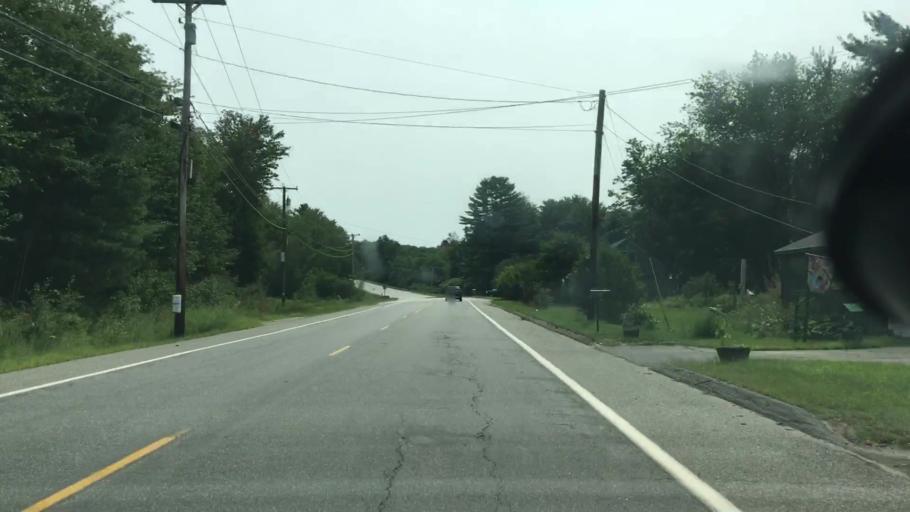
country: US
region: Maine
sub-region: Androscoggin County
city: Livermore Falls
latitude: 44.4569
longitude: -70.1740
